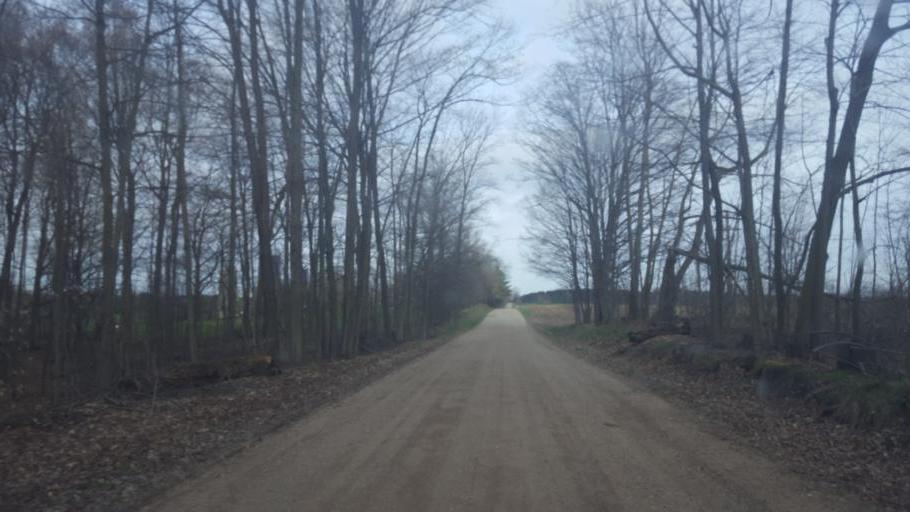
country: US
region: Michigan
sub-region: Isabella County
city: Lake Isabella
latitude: 43.5383
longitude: -85.0747
